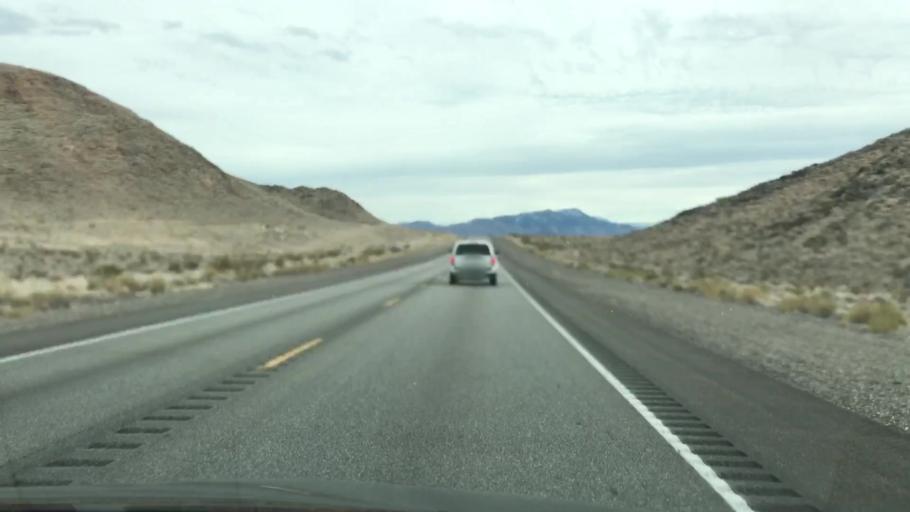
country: US
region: Nevada
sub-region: Nye County
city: Pahrump
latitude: 36.5840
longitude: -116.2099
